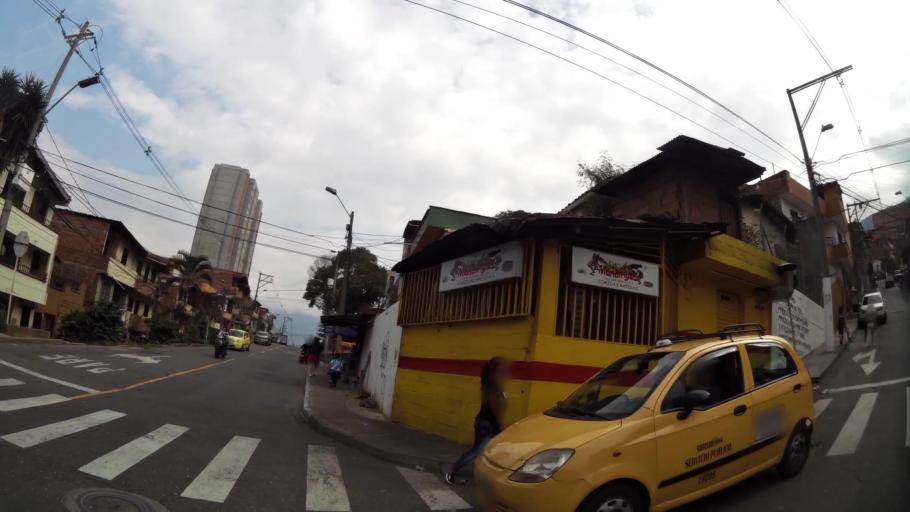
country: CO
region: Antioquia
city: Medellin
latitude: 6.2843
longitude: -75.5527
